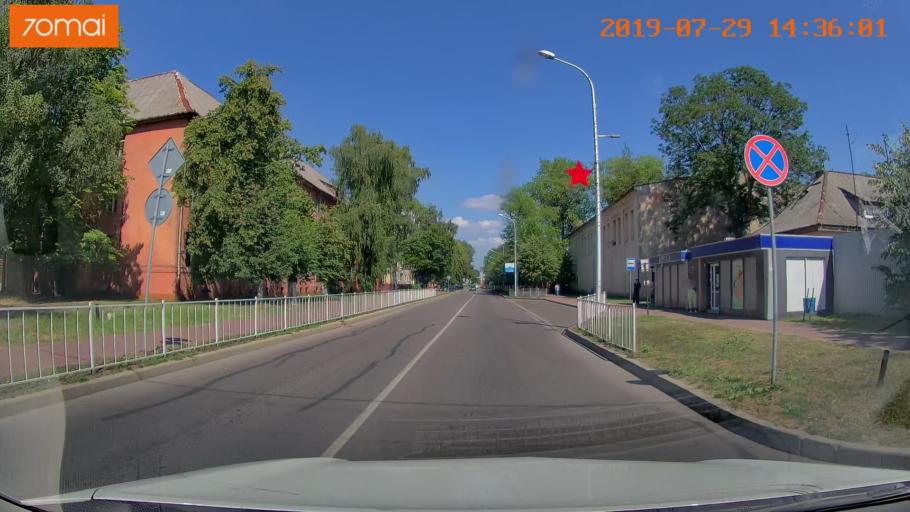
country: RU
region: Kaliningrad
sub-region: Gorod Kaliningrad
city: Baltiysk
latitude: 54.6451
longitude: 19.8967
